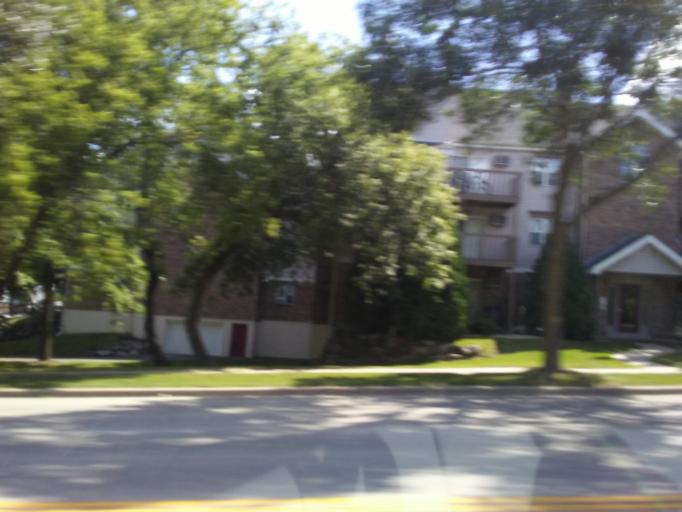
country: US
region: Wisconsin
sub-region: Dane County
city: Middleton
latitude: 43.0501
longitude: -89.5179
